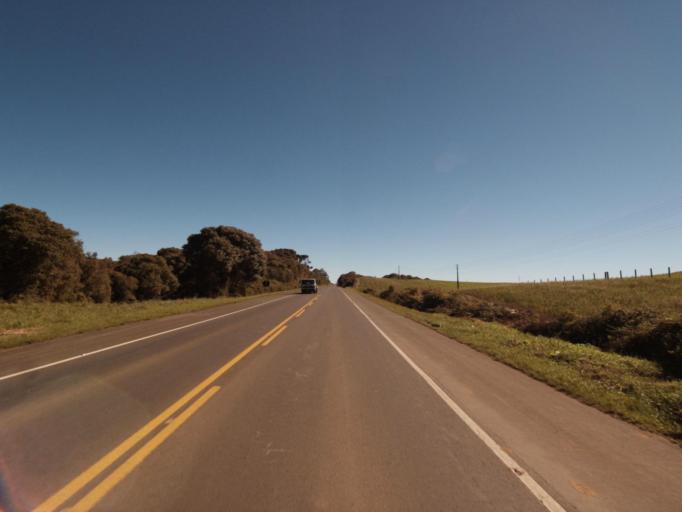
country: BR
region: Santa Catarina
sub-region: Xanxere
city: Xanxere
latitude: -26.8655
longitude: -52.2085
